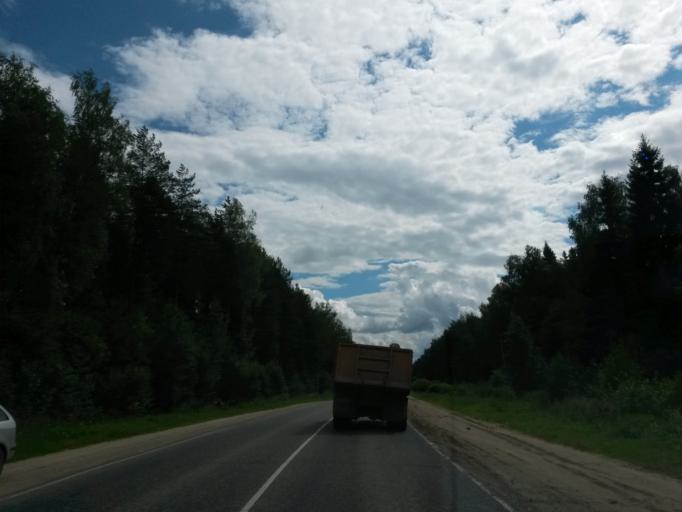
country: RU
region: Ivanovo
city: Novo-Talitsy
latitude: 57.0526
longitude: 40.7345
